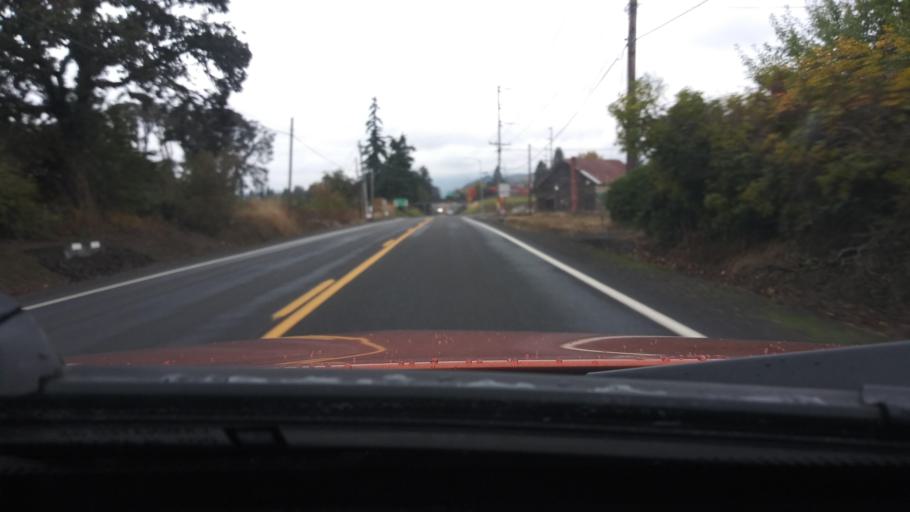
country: US
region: Oregon
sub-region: Washington County
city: Banks
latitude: 45.6064
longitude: -123.1145
